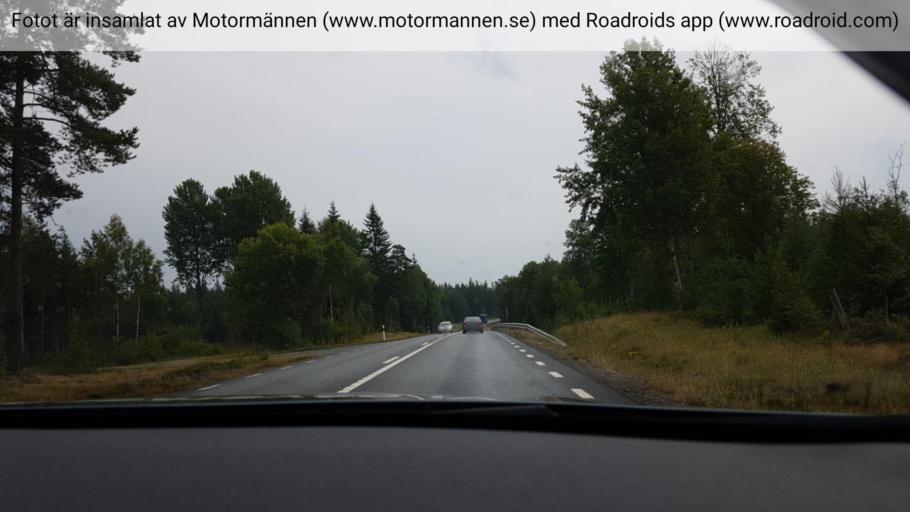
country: SE
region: Joenkoeping
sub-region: Savsjo Kommun
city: Vrigstad
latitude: 57.4018
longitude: 14.3657
